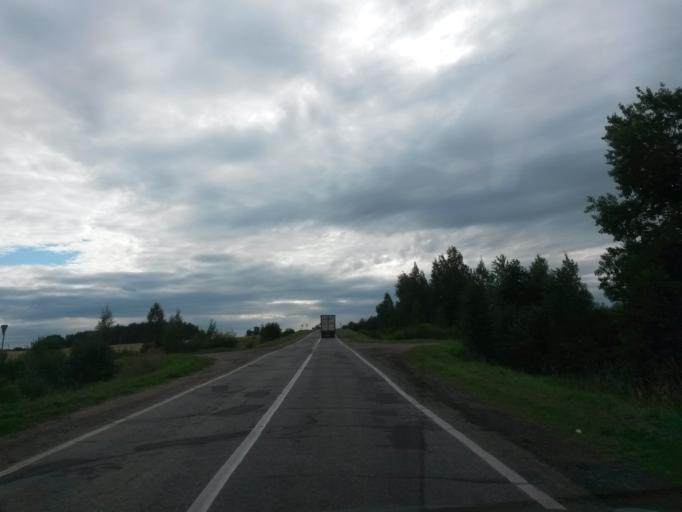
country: RU
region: Jaroslavl
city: Gavrilov-Yam
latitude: 57.3080
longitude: 39.9133
